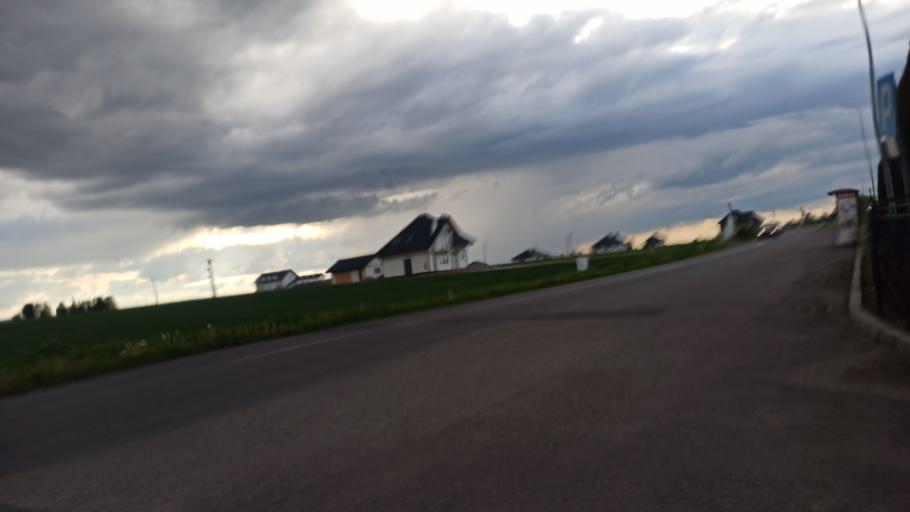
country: PL
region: Subcarpathian Voivodeship
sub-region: Powiat jaroslawski
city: Sosnica
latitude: 49.9230
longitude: 22.8523
